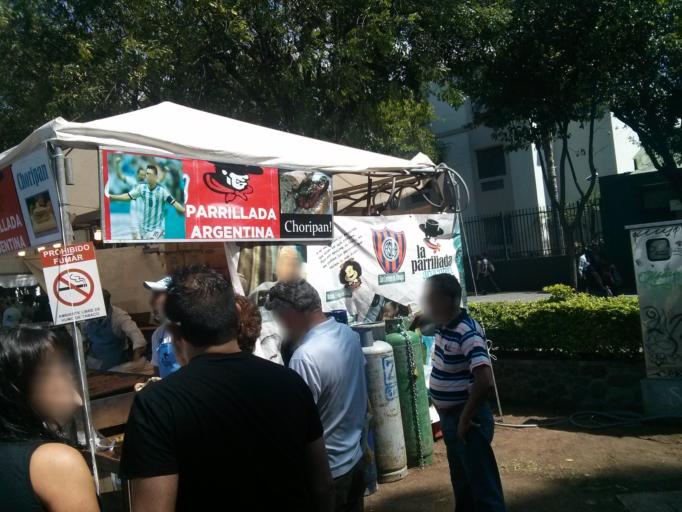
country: CR
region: San Jose
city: San Jose
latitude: 9.9358
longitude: -84.0745
